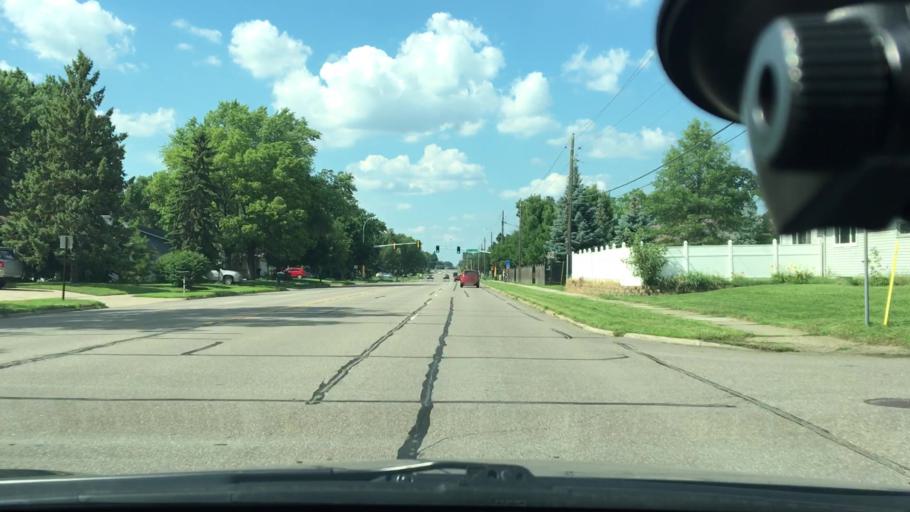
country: US
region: Minnesota
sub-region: Hennepin County
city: New Hope
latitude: 45.0423
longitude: -93.3803
